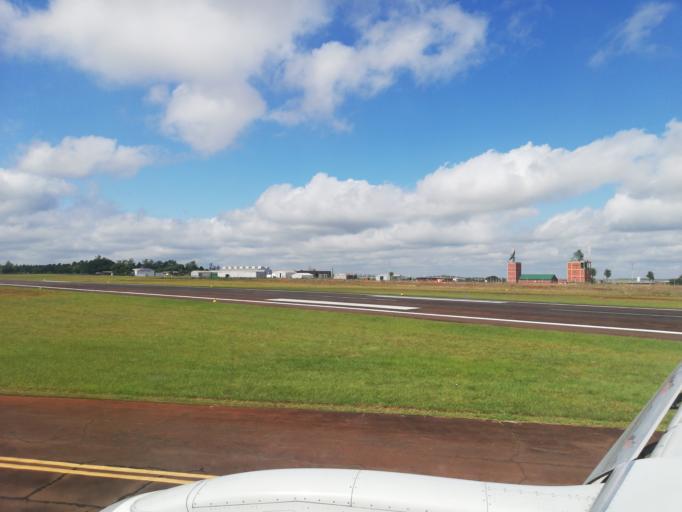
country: AR
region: Misiones
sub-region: Departamento de Capital
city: Posadas
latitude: -27.3900
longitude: -55.9696
